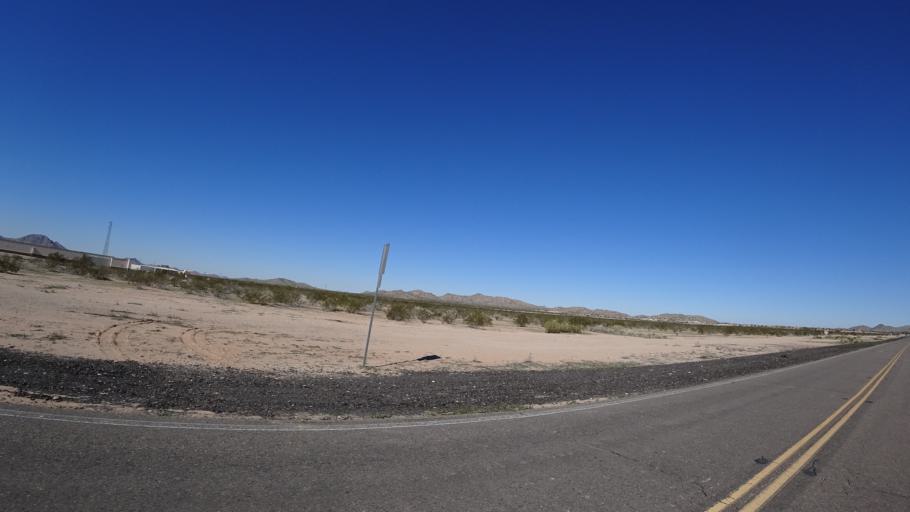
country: US
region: Arizona
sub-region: Maricopa County
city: Buckeye
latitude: 33.2942
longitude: -112.4455
